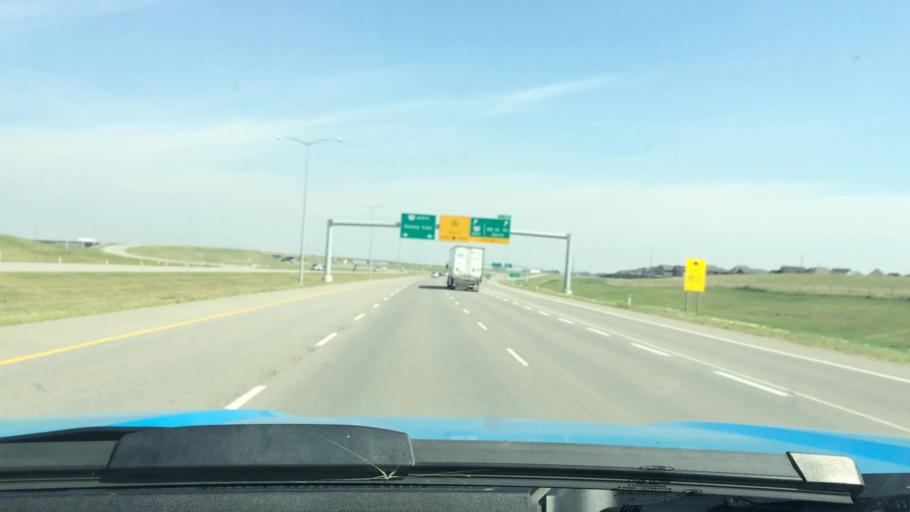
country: CA
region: Alberta
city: Chestermere
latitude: 50.9066
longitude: -113.9261
